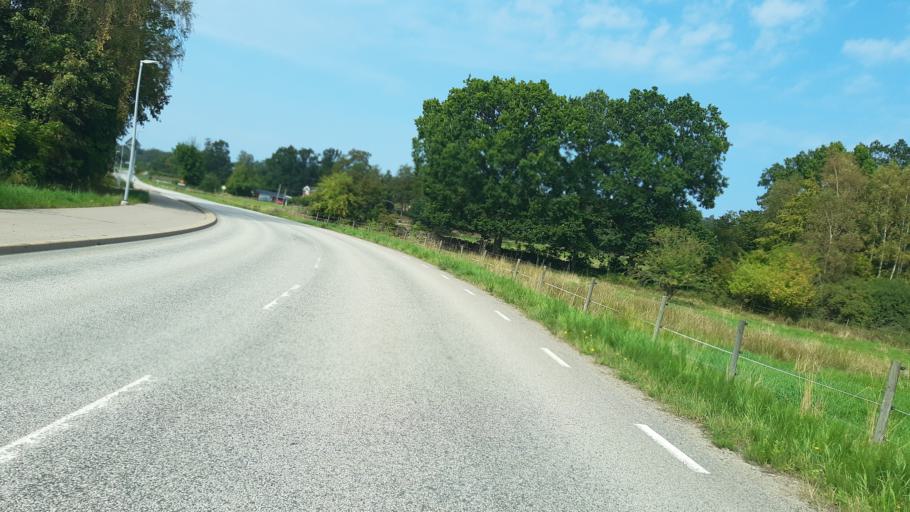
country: SE
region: Blekinge
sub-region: Ronneby Kommun
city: Ronneby
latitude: 56.1781
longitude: 15.2803
